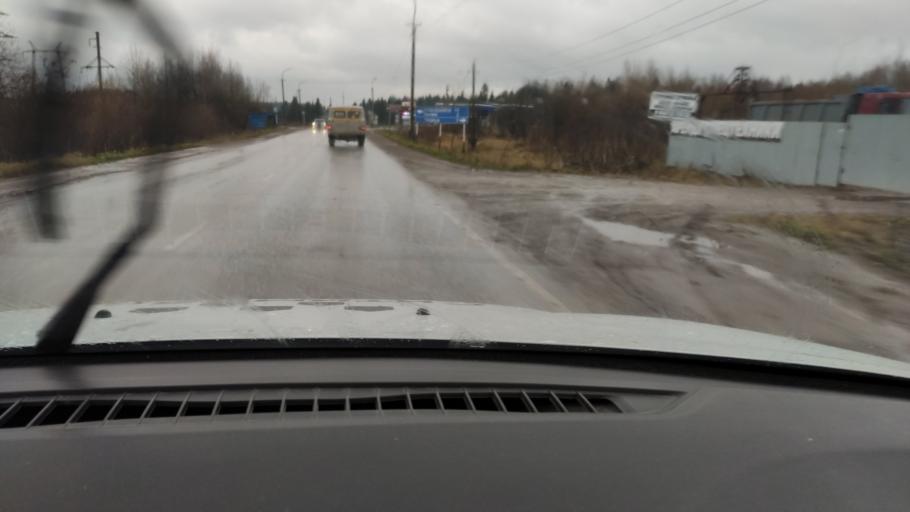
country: RU
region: Perm
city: Sylva
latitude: 58.0261
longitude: 56.7356
